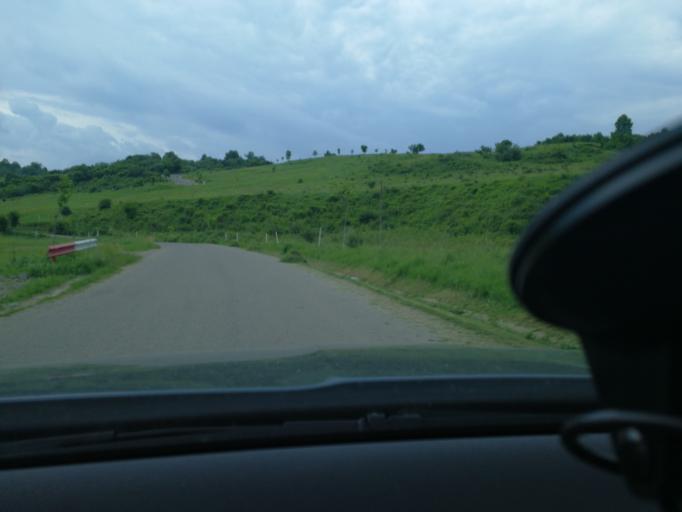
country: RO
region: Prahova
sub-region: Comuna Cornu
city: Cornu de Jos
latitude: 45.1481
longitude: 25.7256
